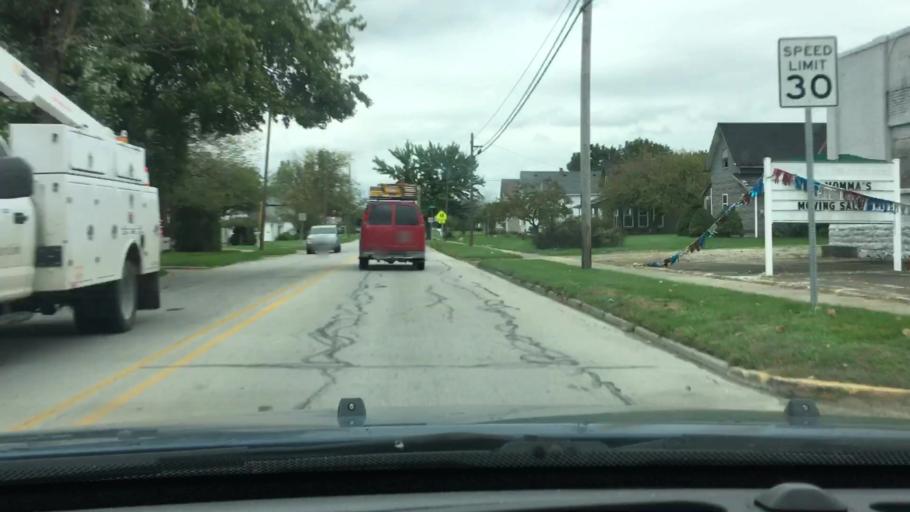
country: US
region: Indiana
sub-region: Jay County
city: Portland
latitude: 40.4216
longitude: -84.9775
